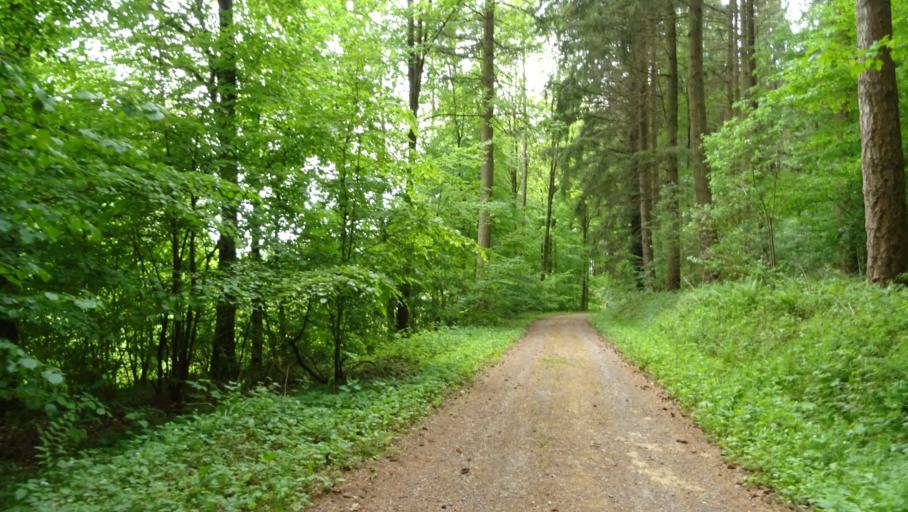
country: DE
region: Baden-Wuerttemberg
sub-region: Karlsruhe Region
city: Neckargerach
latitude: 49.3810
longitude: 9.0873
